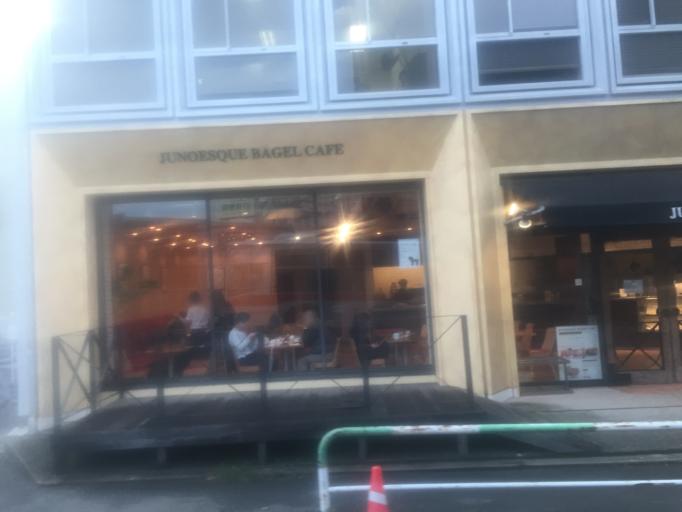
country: JP
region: Tokyo
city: Tokyo
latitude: 35.6067
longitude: 139.6666
